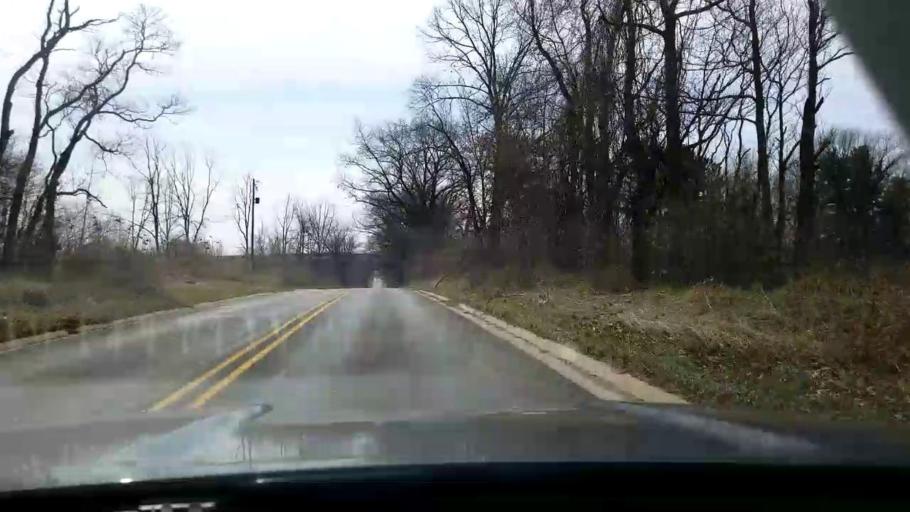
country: US
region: Michigan
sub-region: Jackson County
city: Spring Arbor
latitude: 42.2116
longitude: -84.5213
